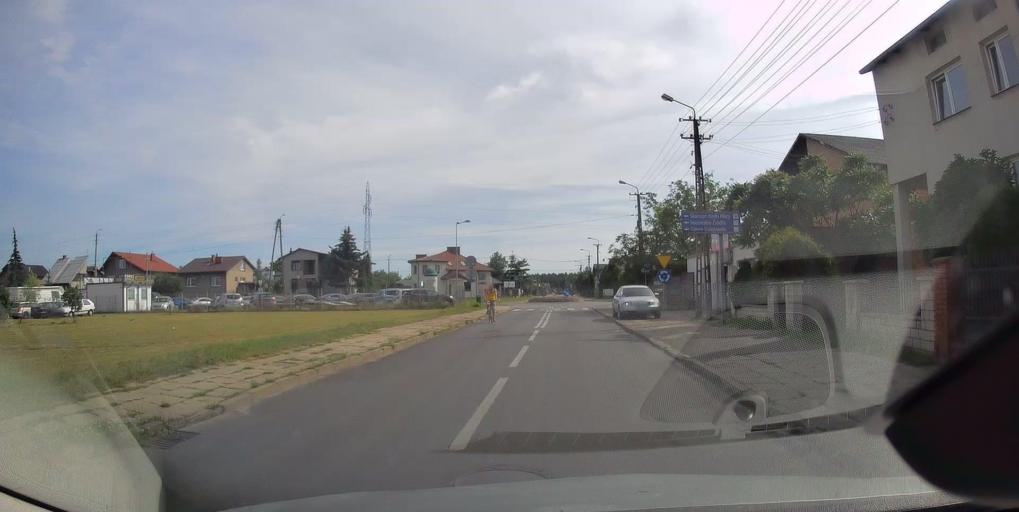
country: PL
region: Lodz Voivodeship
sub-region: Powiat tomaszowski
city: Tomaszow Mazowiecki
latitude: 51.5221
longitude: 19.9969
